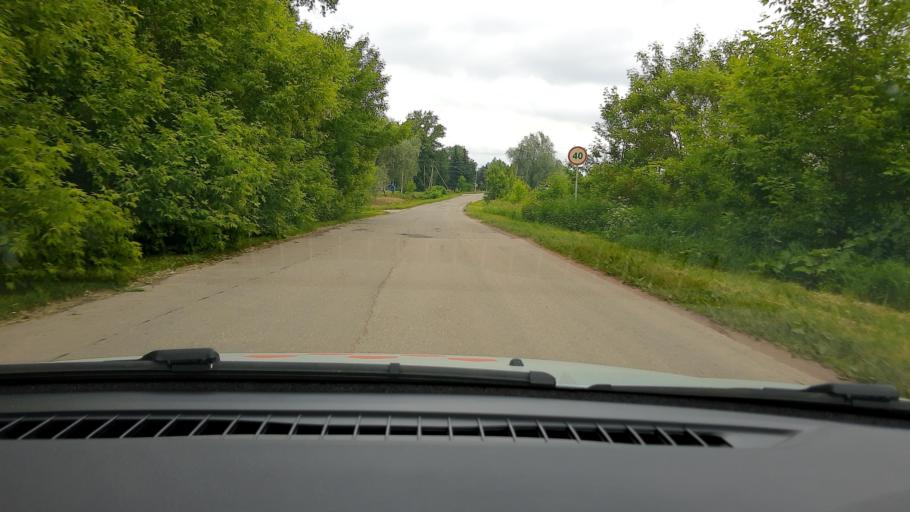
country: RU
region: Nizjnij Novgorod
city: Bogorodsk
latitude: 56.0701
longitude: 43.5047
